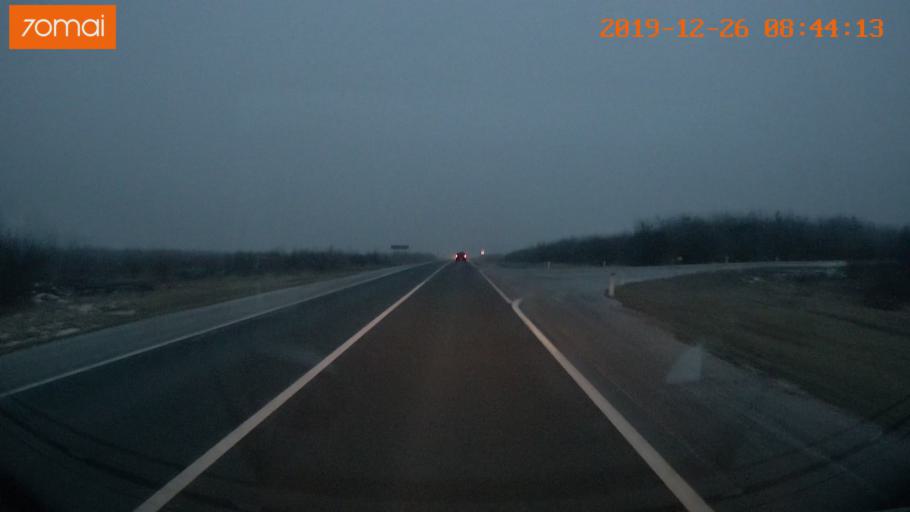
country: RU
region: Jaroslavl
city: Prechistoye
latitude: 58.5829
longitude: 40.3493
